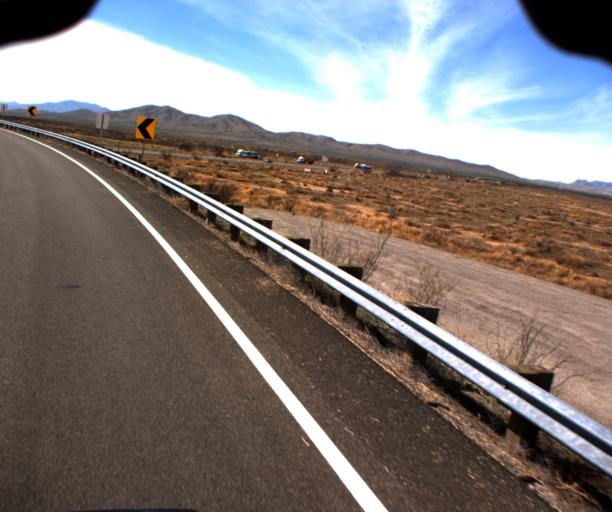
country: US
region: Arizona
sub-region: Cochise County
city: Willcox
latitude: 32.1780
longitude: -109.9499
